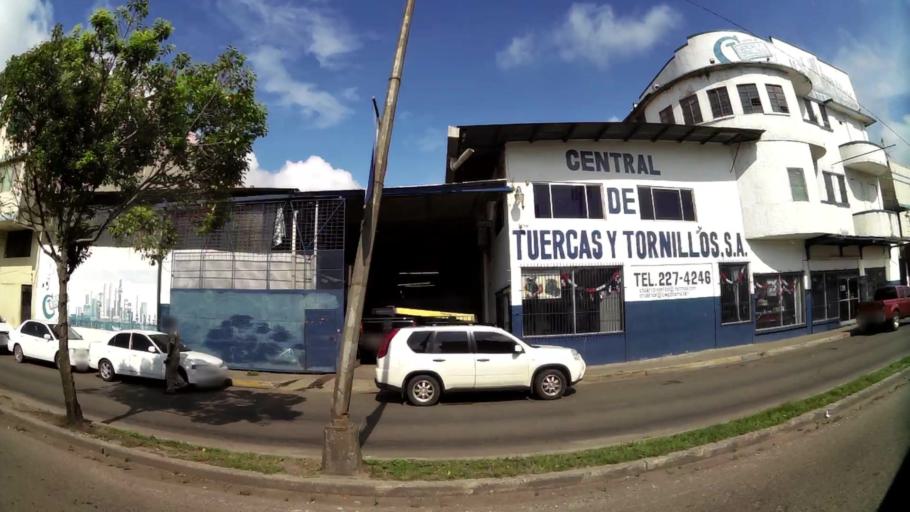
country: PA
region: Panama
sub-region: Distrito de Panama
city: Ancon
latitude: 8.9677
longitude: -79.5419
